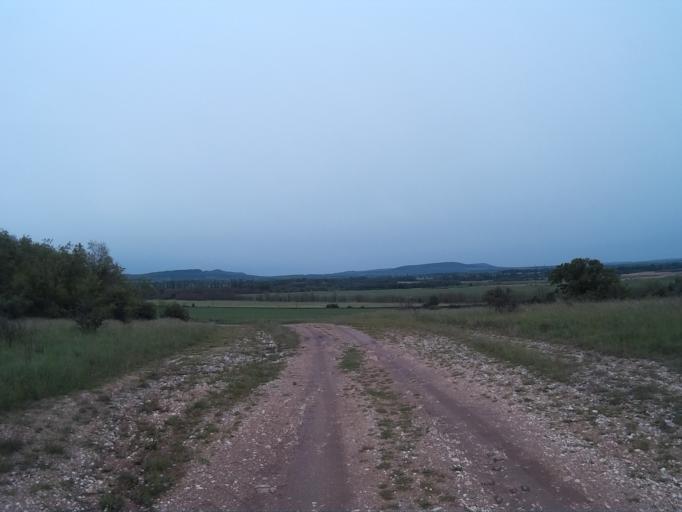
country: HU
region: Veszprem
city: Sumeg
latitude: 46.9606
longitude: 17.2889
